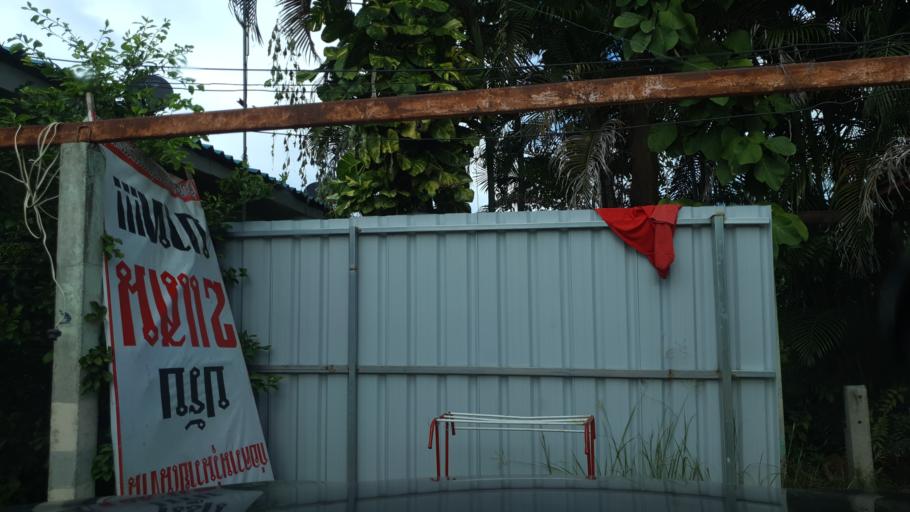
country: TH
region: Sukhothai
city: Thung Saliam
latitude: 17.3284
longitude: 99.5760
